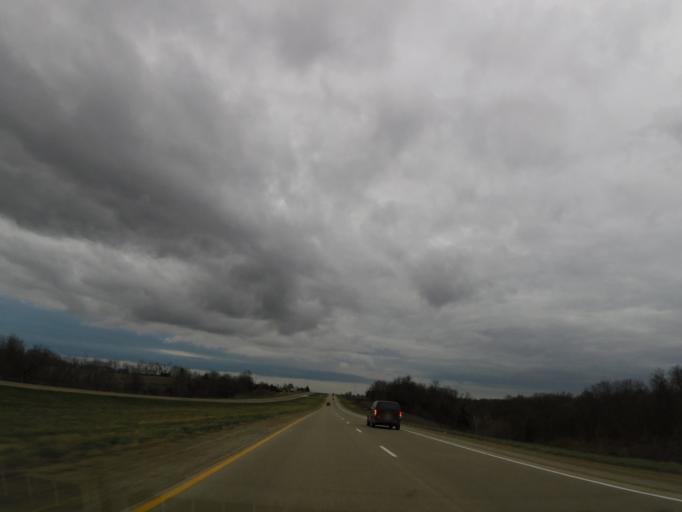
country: US
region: Iowa
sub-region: Henry County
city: Mount Pleasant
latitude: 40.8402
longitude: -91.5649
